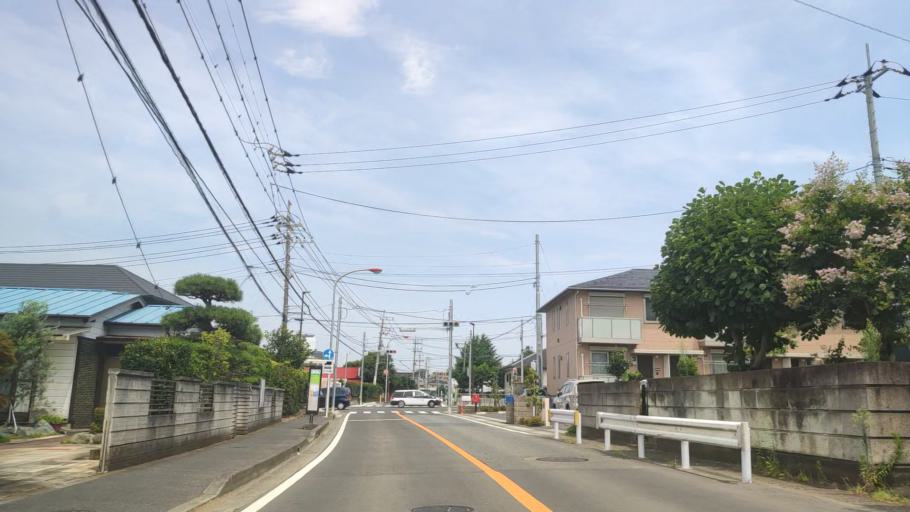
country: JP
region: Kanagawa
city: Atsugi
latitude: 35.4381
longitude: 139.3943
